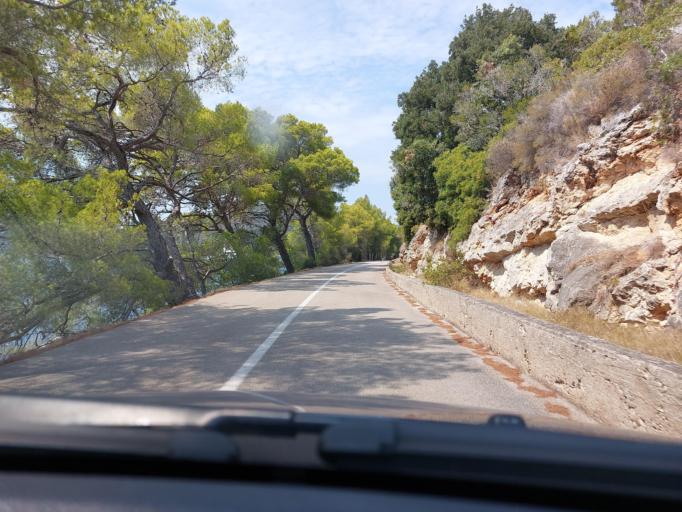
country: HR
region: Dubrovacko-Neretvanska
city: Smokvica
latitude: 42.7563
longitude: 16.8235
